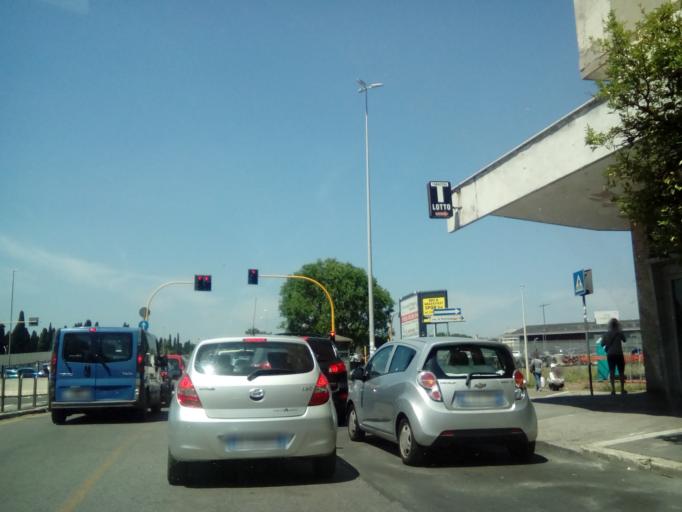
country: IT
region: Latium
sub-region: Citta metropolitana di Roma Capitale
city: Rome
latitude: 41.9083
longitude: 12.5352
